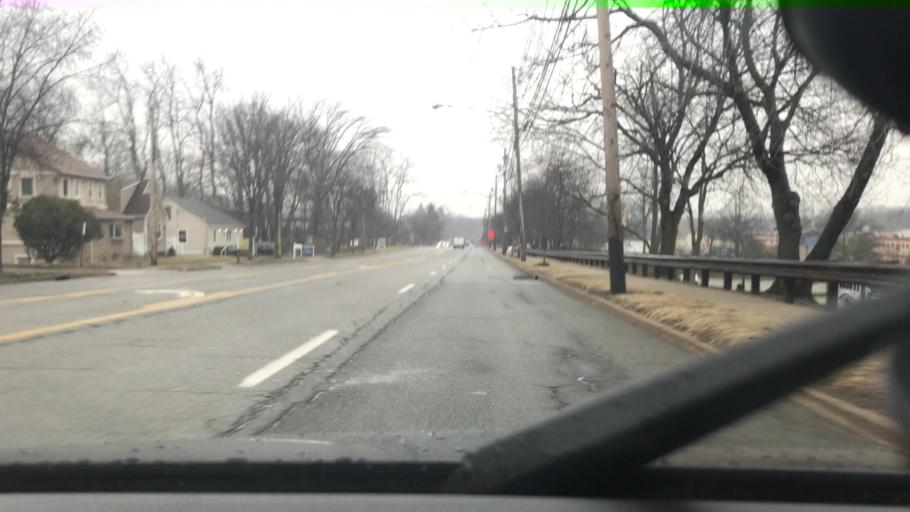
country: US
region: New Jersey
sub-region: Morris County
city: Morris Plains
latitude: 40.8089
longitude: -74.4601
